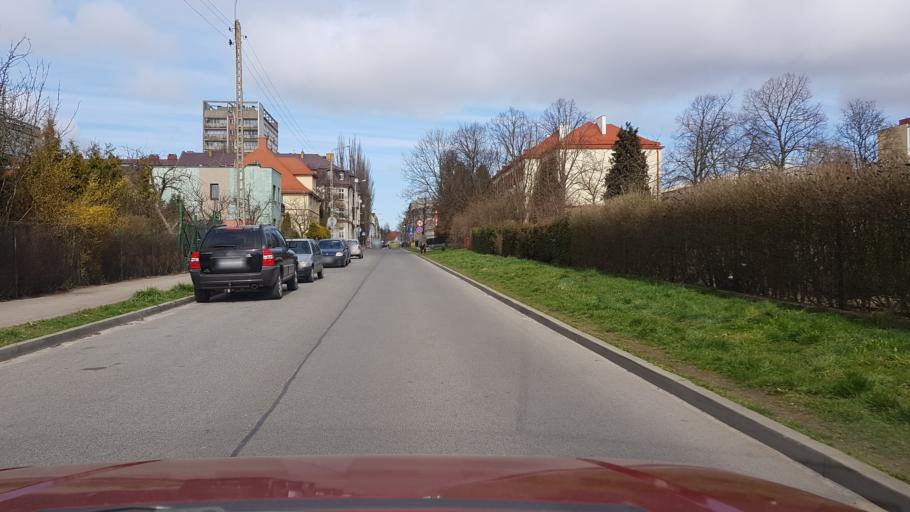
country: PL
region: West Pomeranian Voivodeship
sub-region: Koszalin
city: Koszalin
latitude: 54.1883
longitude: 16.2025
